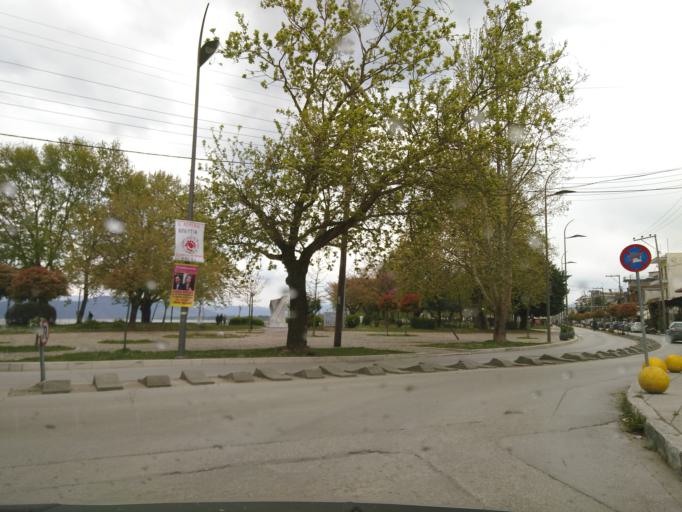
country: GR
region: Epirus
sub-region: Nomos Ioanninon
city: Ioannina
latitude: 39.6677
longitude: 20.8588
